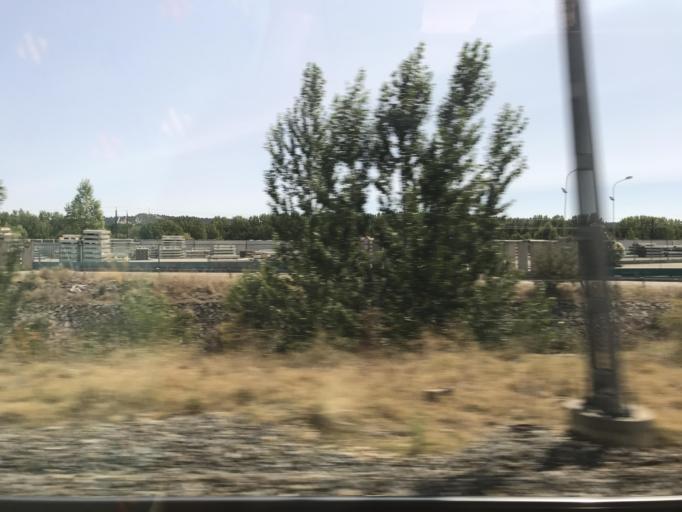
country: ES
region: Castille and Leon
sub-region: Provincia de Palencia
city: Venta de Banos
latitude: 41.9111
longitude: -4.5036
